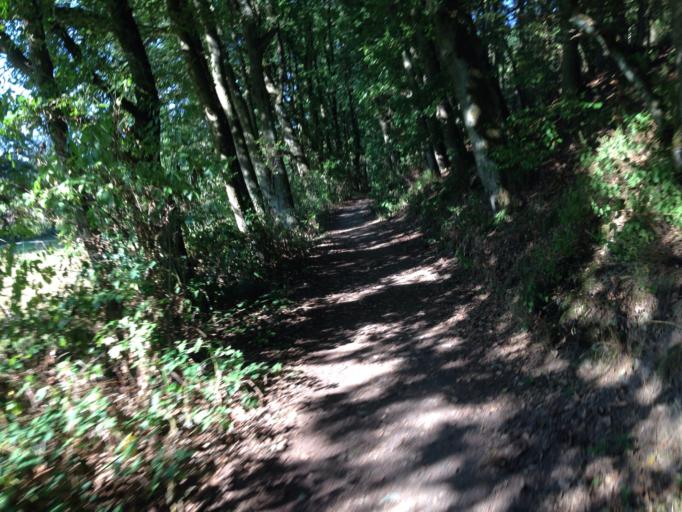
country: DE
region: Hesse
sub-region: Regierungsbezirk Giessen
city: Heuchelheim
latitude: 50.6241
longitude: 8.6456
